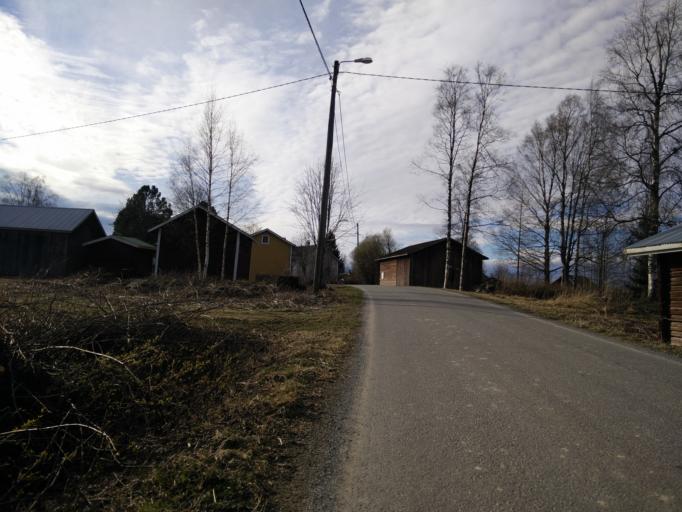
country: FI
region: Pirkanmaa
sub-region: Tampere
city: Orivesi
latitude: 61.7100
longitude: 24.3312
